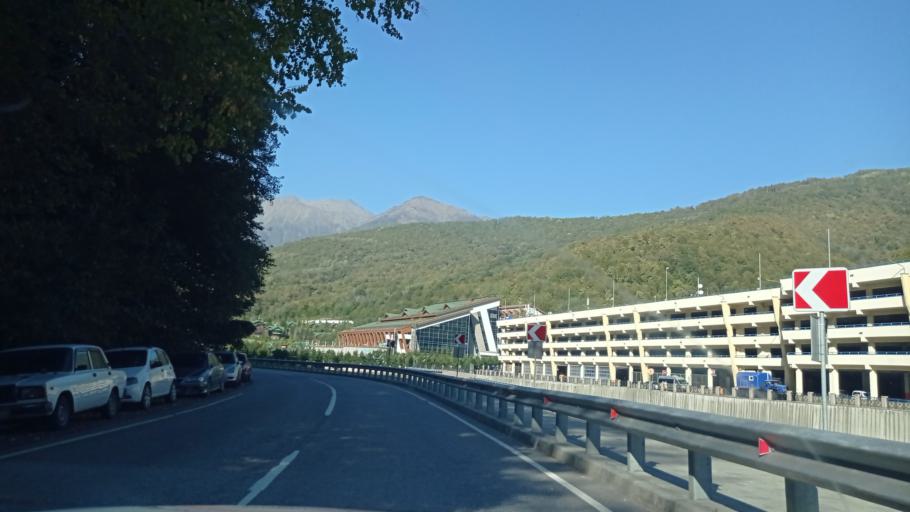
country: RU
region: Krasnodarskiy
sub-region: Sochi City
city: Krasnaya Polyana
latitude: 43.6827
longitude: 40.2785
